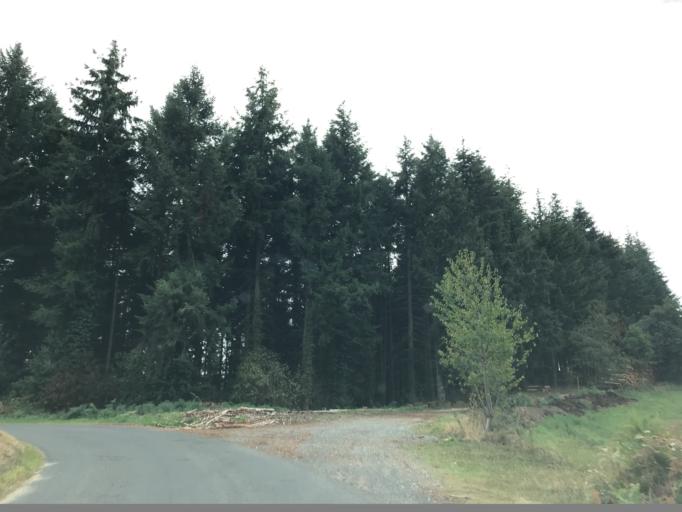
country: FR
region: Auvergne
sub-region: Departement du Puy-de-Dome
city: Escoutoux
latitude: 45.8234
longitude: 3.5877
